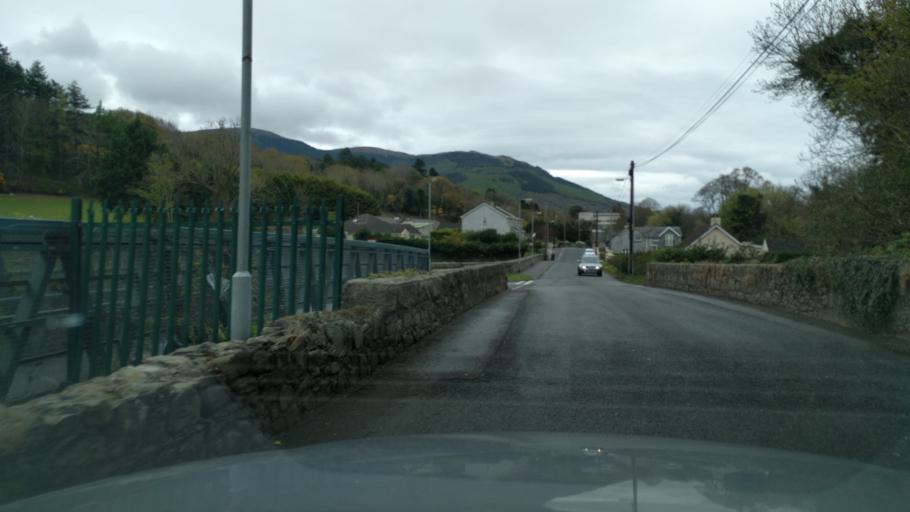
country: GB
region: Northern Ireland
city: Rostrevor
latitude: 54.1082
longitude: -6.2047
